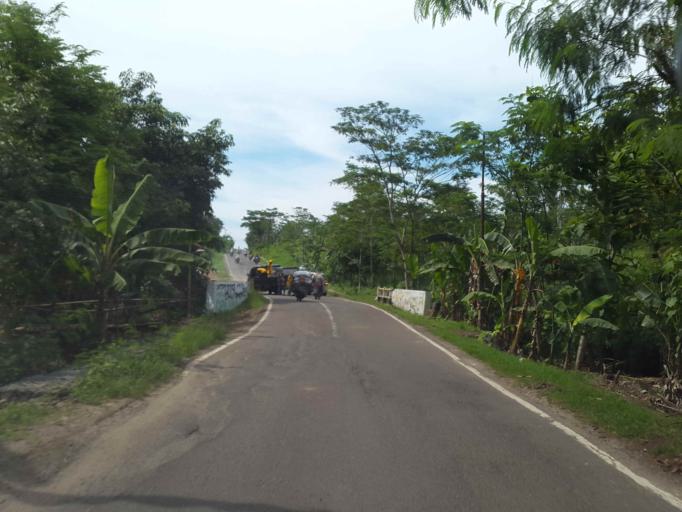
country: ID
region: Banten
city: Citeureup
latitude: -6.5179
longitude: 105.6835
